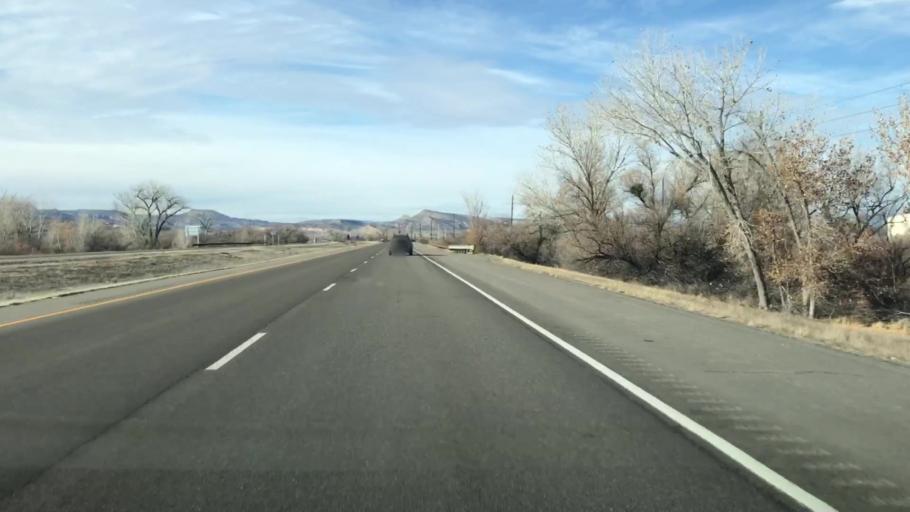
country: US
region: Colorado
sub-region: Mesa County
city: Fruita
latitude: 39.1600
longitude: -108.7554
